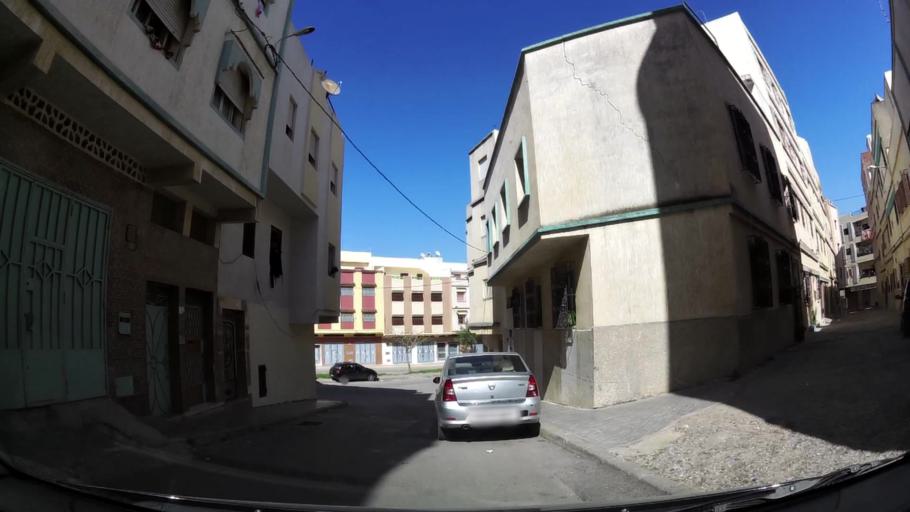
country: MA
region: Tanger-Tetouan
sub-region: Tanger-Assilah
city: Tangier
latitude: 35.7510
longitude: -5.8081
